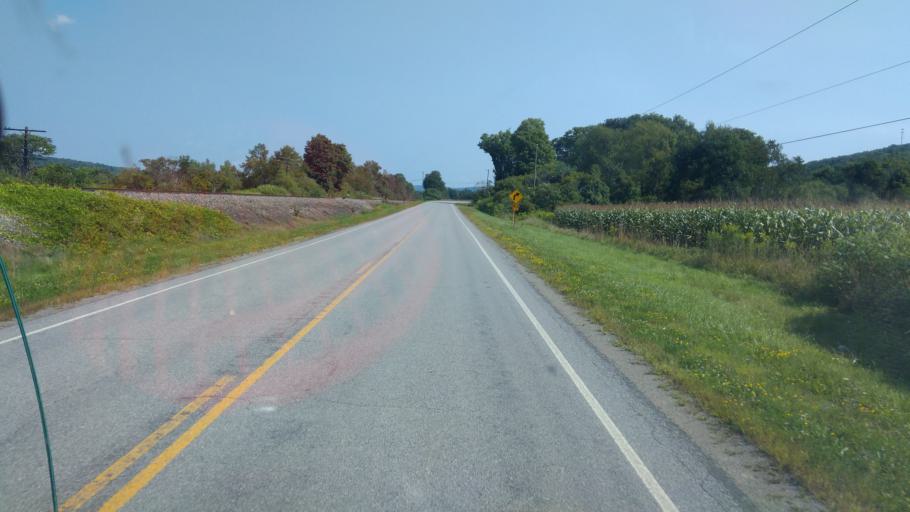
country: US
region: New York
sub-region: Allegany County
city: Belmont
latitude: 42.2358
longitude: -78.0826
